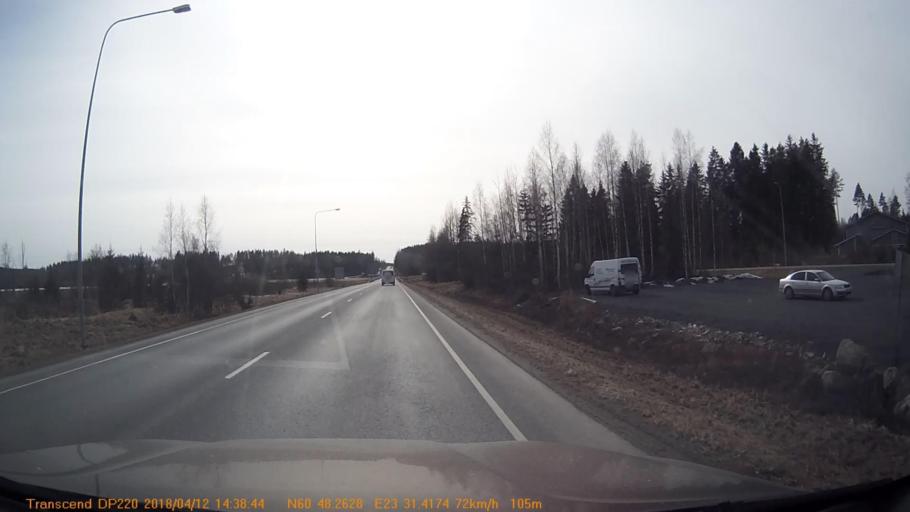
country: FI
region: Haeme
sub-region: Forssa
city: Jokioinen
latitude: 60.8032
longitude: 23.5215
